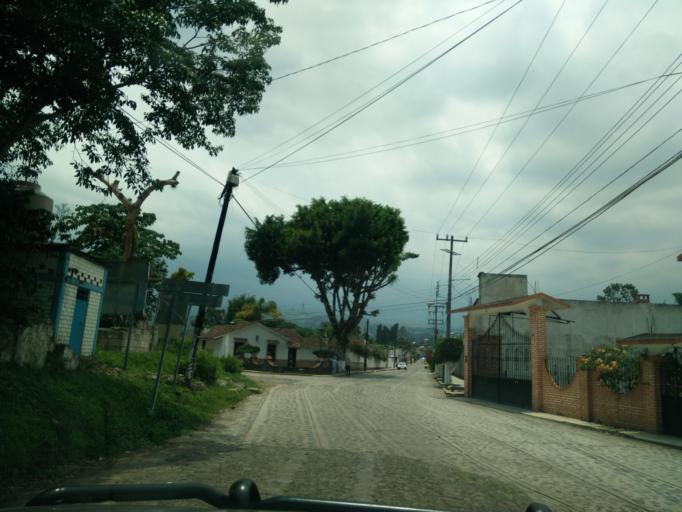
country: MX
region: Veracruz
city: Xico
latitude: 19.4161
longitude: -96.9976
